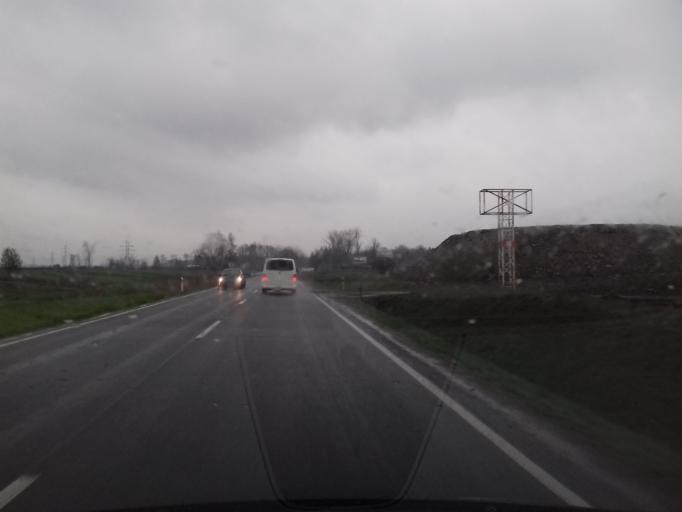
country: PL
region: Lesser Poland Voivodeship
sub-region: Powiat nowosadecki
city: Stary Sacz
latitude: 49.5551
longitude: 20.6548
